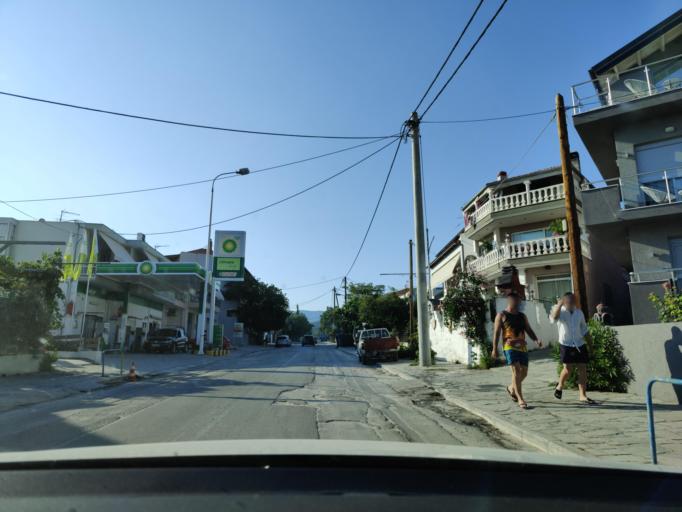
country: GR
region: East Macedonia and Thrace
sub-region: Nomos Kavalas
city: Limenaria
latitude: 40.6116
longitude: 24.6068
